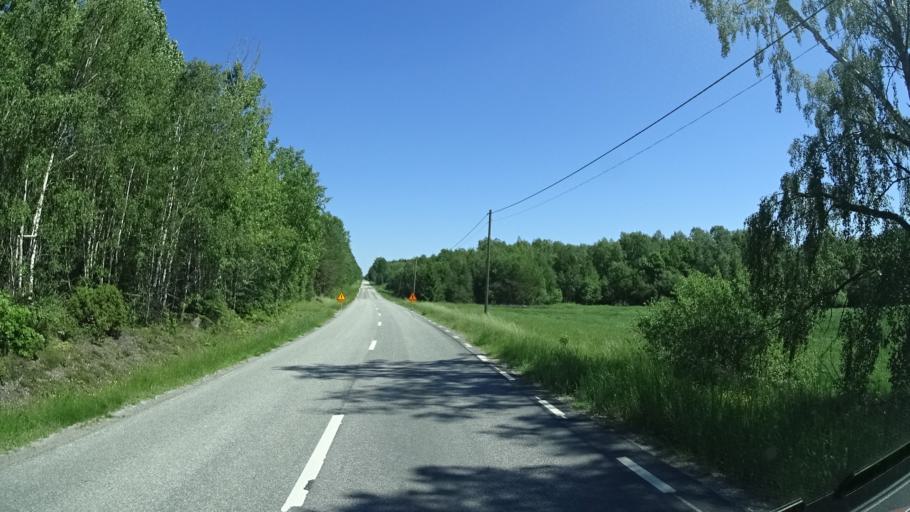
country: SE
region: Stockholm
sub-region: Vallentuna Kommun
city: Vallentuna
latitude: 59.5983
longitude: 18.1198
